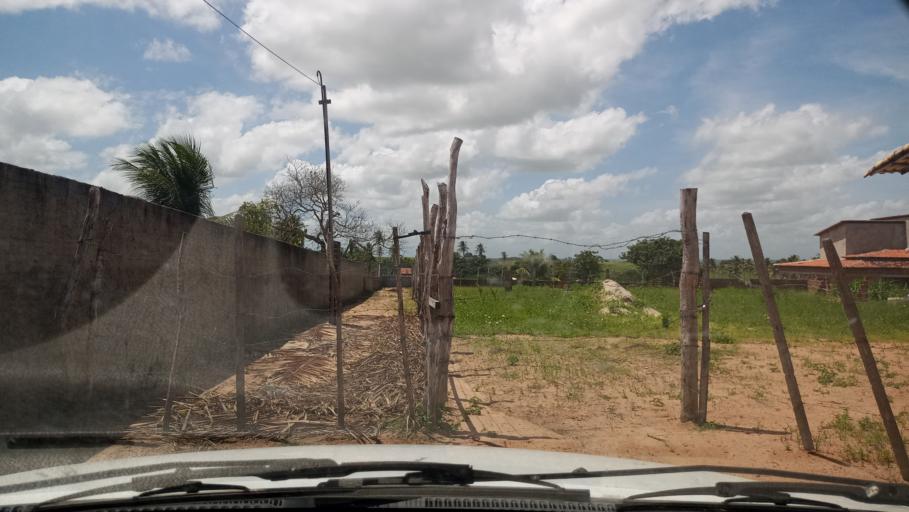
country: BR
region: Rio Grande do Norte
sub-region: Brejinho
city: Brejinho
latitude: -6.2651
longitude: -35.3703
